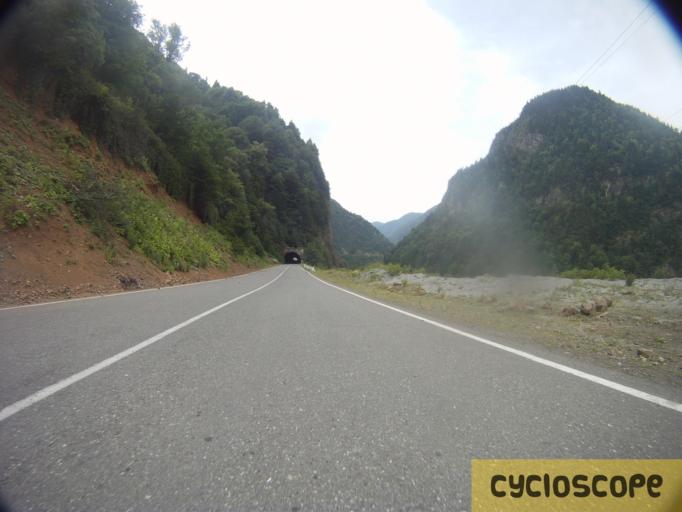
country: GE
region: Samegrelo and Zemo Svaneti
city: Jvari
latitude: 42.9128
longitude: 42.0723
